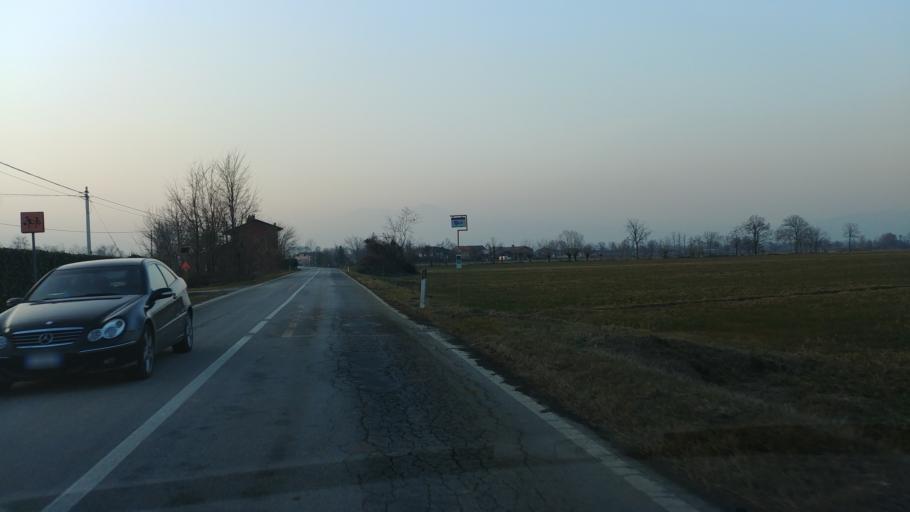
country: IT
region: Piedmont
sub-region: Provincia di Cuneo
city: Roata Rossi
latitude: 44.4251
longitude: 7.5237
